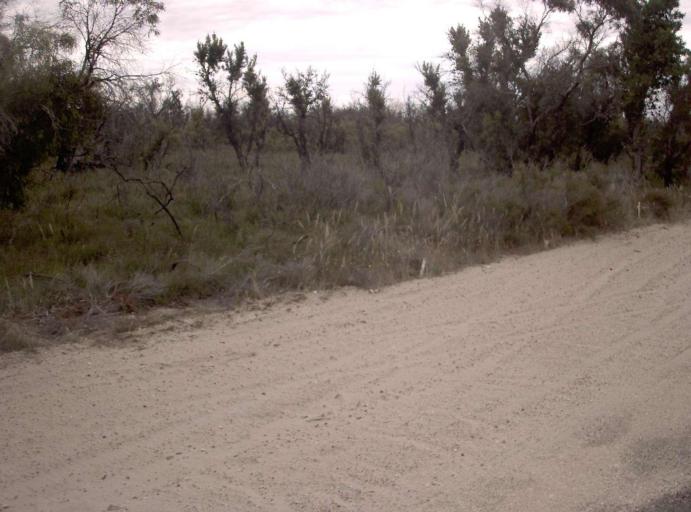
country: AU
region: Victoria
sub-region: East Gippsland
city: Bairnsdale
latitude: -38.1165
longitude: 147.4613
